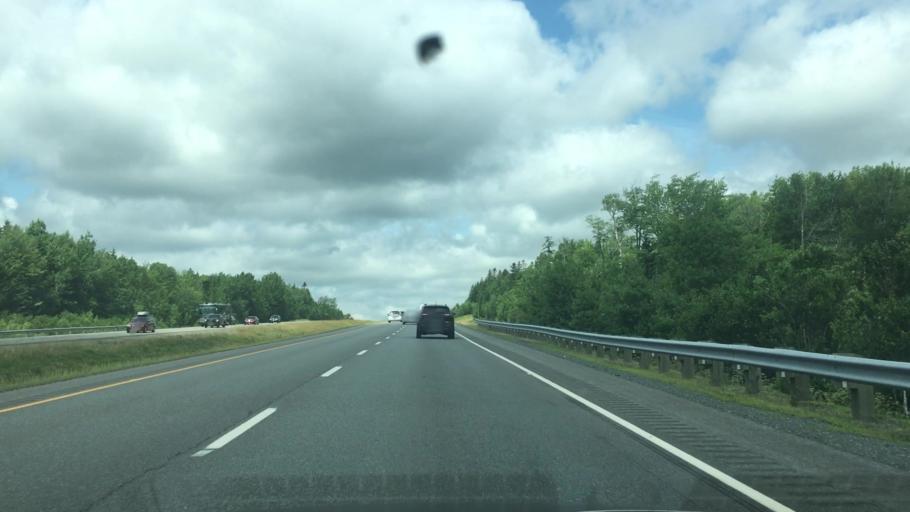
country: CA
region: Nova Scotia
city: Springhill
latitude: 45.7038
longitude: -64.0298
